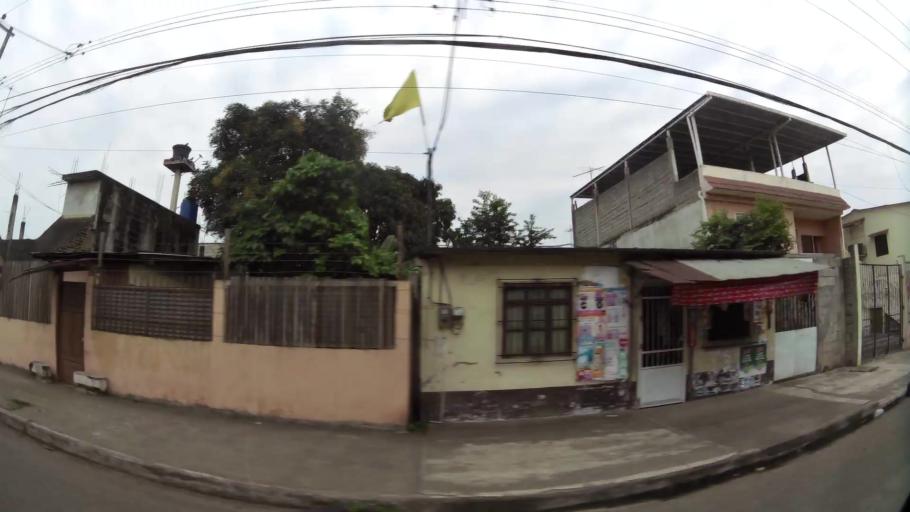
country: EC
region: El Oro
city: Machala
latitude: -3.2669
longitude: -79.9386
